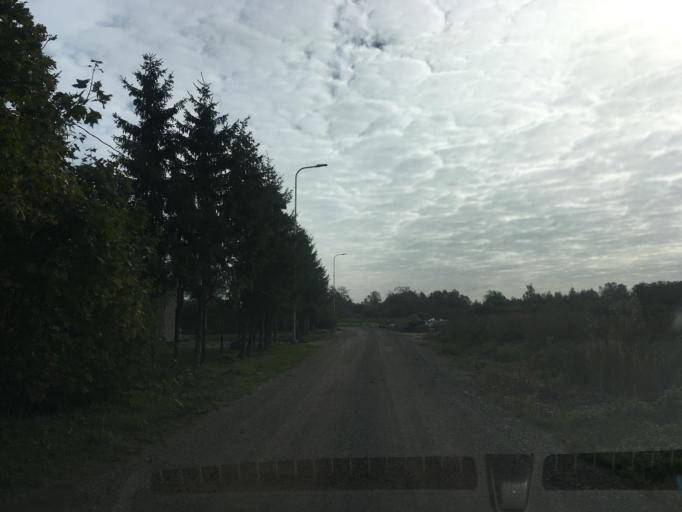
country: EE
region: Harju
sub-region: Joelaehtme vald
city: Loo
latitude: 59.4425
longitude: 24.9763
